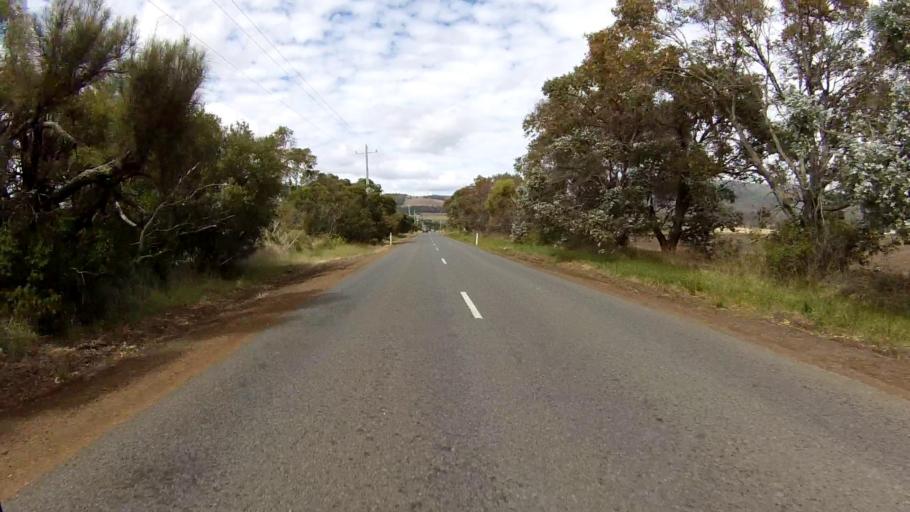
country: AU
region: Tasmania
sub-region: Clarence
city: Cambridge
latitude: -42.7530
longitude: 147.4087
